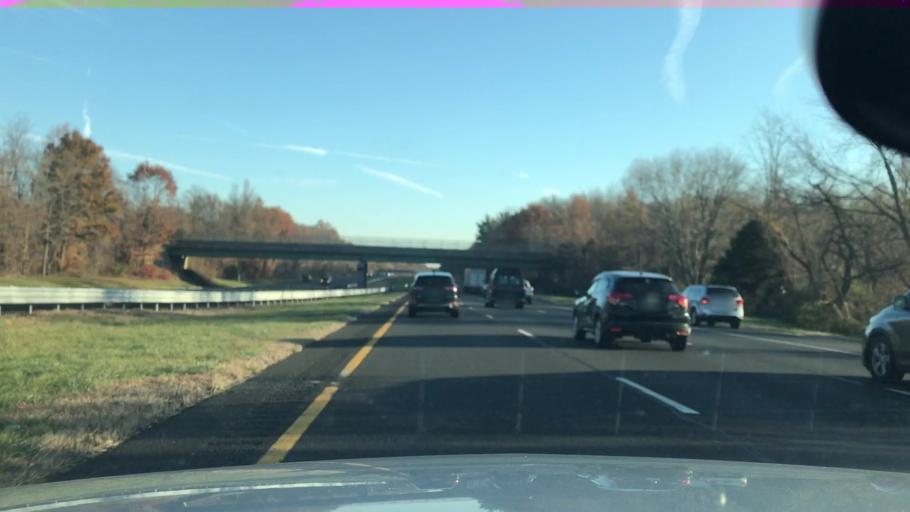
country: US
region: New Jersey
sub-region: Burlington County
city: Roebling
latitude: 40.1045
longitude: -74.7421
